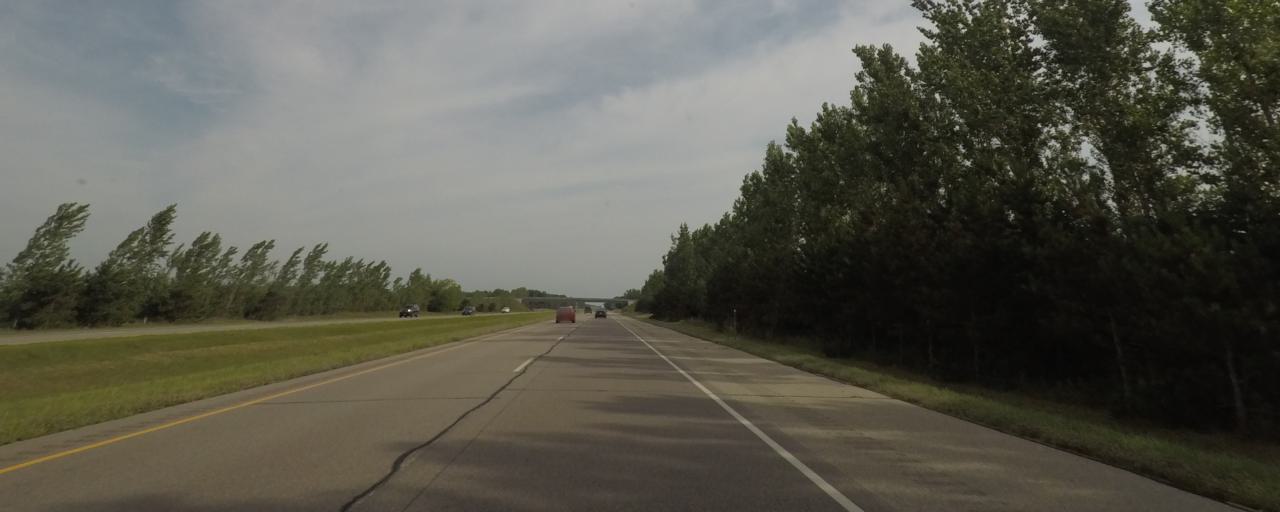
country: US
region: Wisconsin
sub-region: Portage County
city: Plover
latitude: 44.2837
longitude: -89.5233
